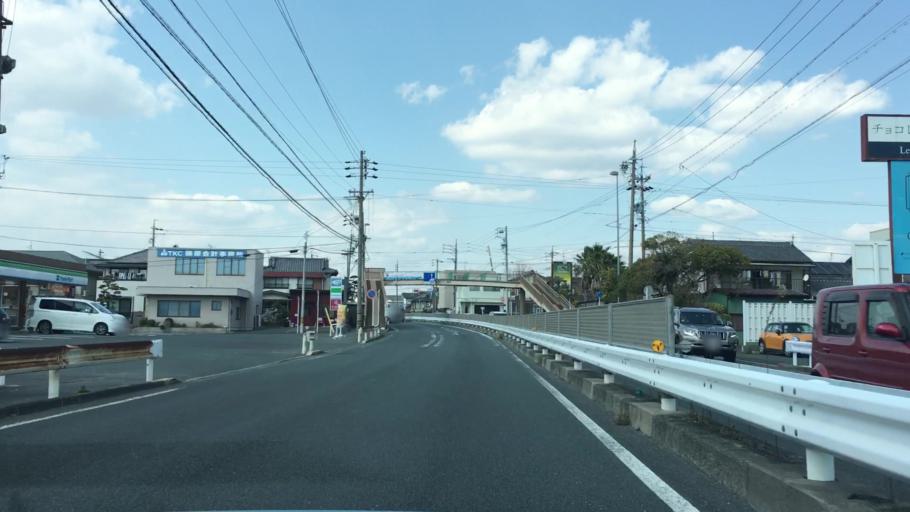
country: JP
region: Aichi
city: Toyohashi
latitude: 34.7537
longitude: 137.4115
